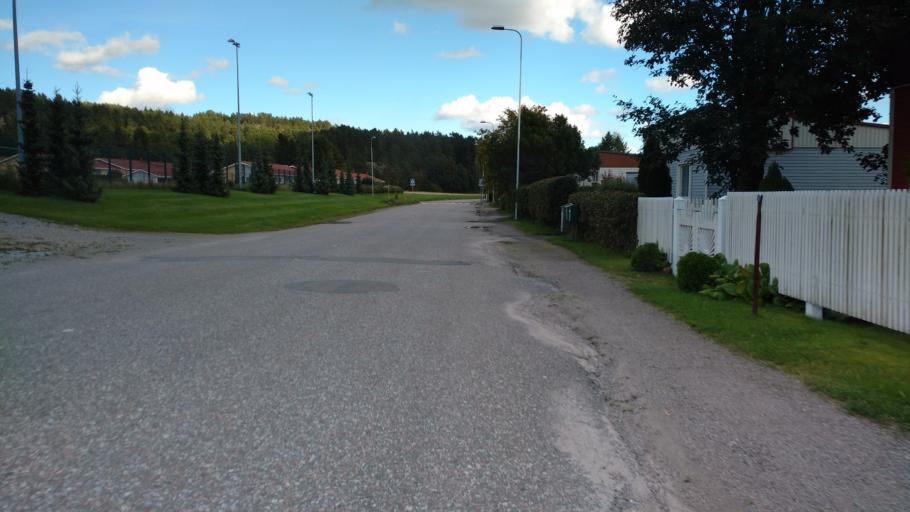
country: FI
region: Varsinais-Suomi
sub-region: Salo
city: Salo
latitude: 60.3810
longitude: 23.1585
